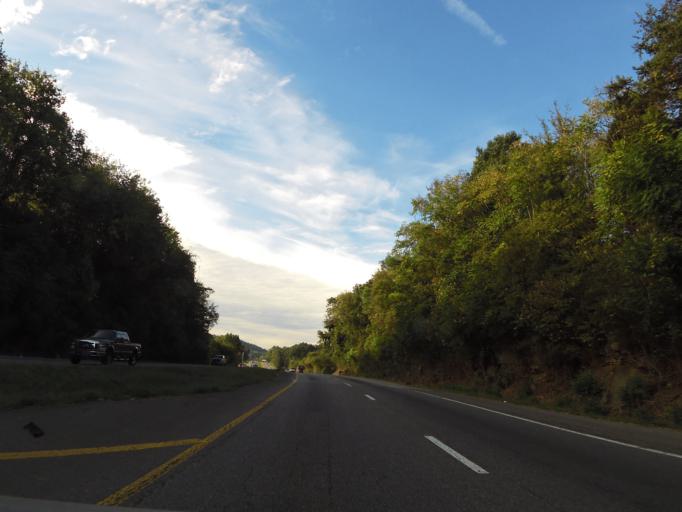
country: US
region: Tennessee
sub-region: Blount County
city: Eagleton Village
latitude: 35.8704
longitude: -83.9595
